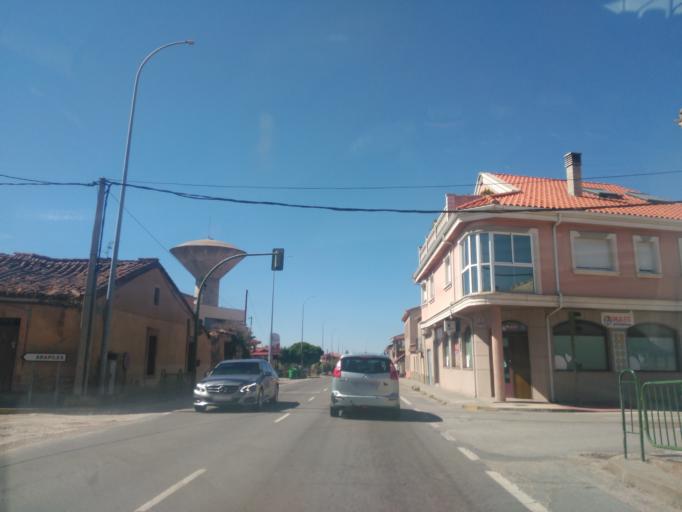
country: ES
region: Castille and Leon
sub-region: Provincia de Salamanca
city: Calvarrasa de Arriba
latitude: 40.9054
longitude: -5.5929
